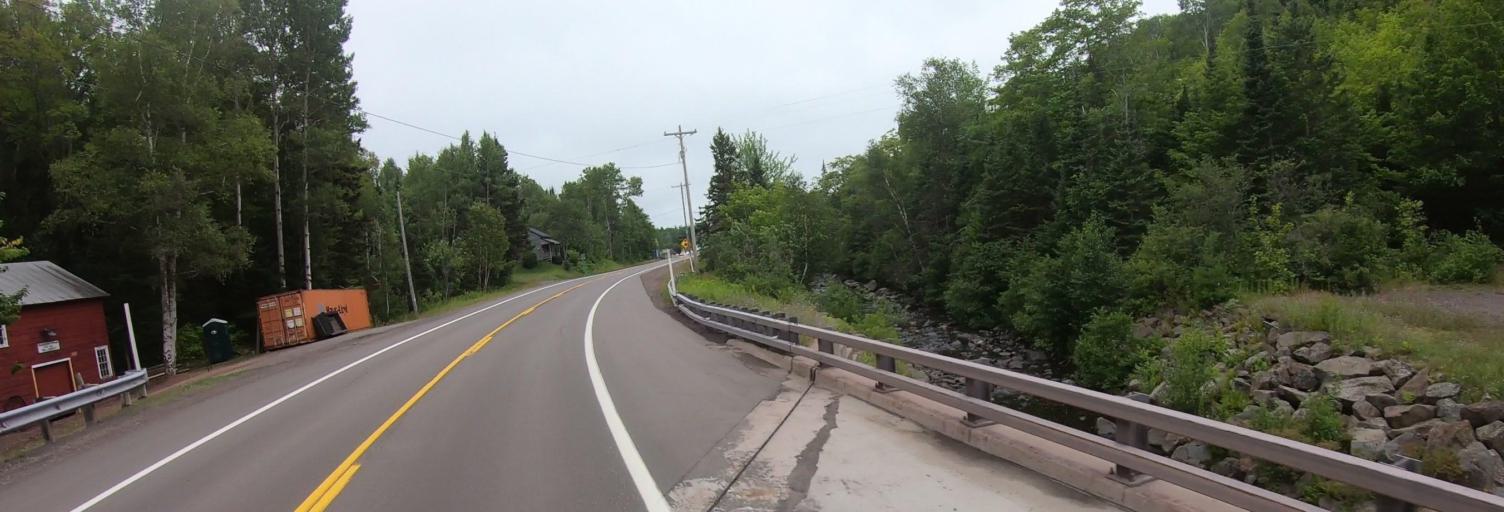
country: US
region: Michigan
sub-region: Keweenaw County
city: Eagle River
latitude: 47.3923
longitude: -88.2767
